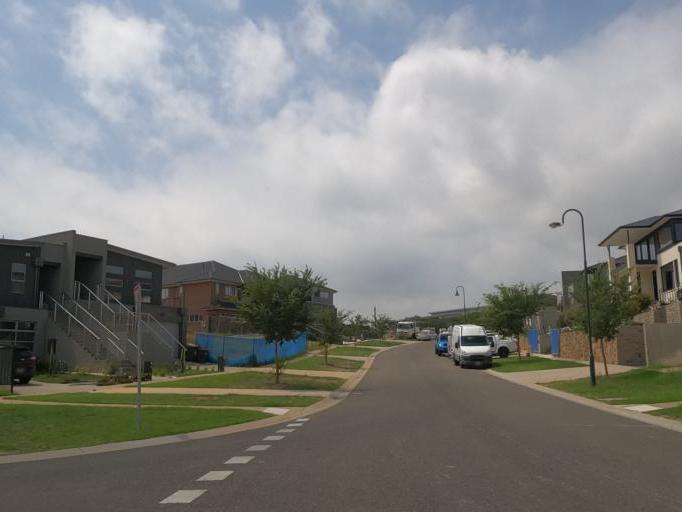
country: AU
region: Victoria
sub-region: Hume
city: Attwood
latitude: -37.6705
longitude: 144.8773
